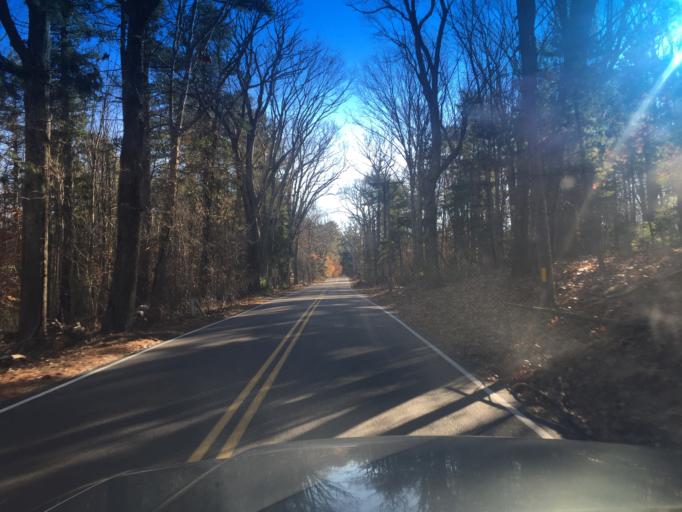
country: US
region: Massachusetts
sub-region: Middlesex County
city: Holliston
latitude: 42.1946
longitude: -71.3890
